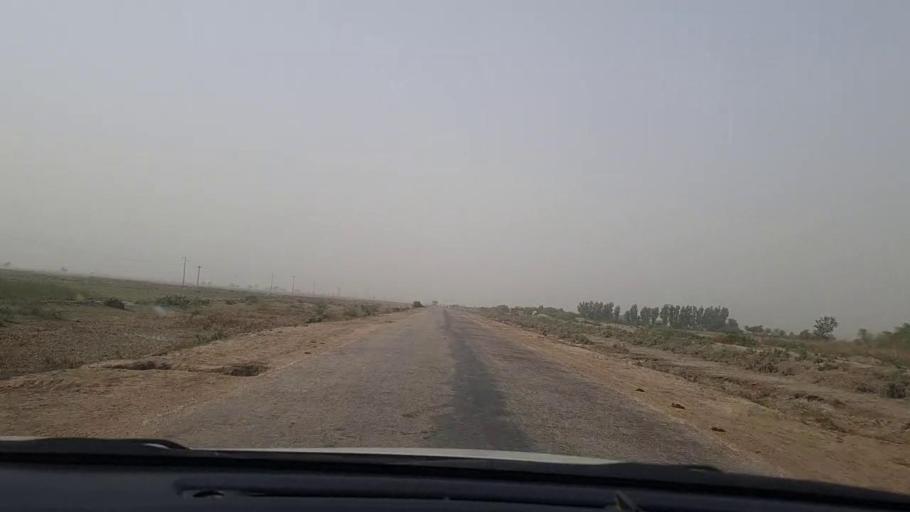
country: PK
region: Sindh
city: Pithoro
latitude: 25.4089
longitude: 69.3921
